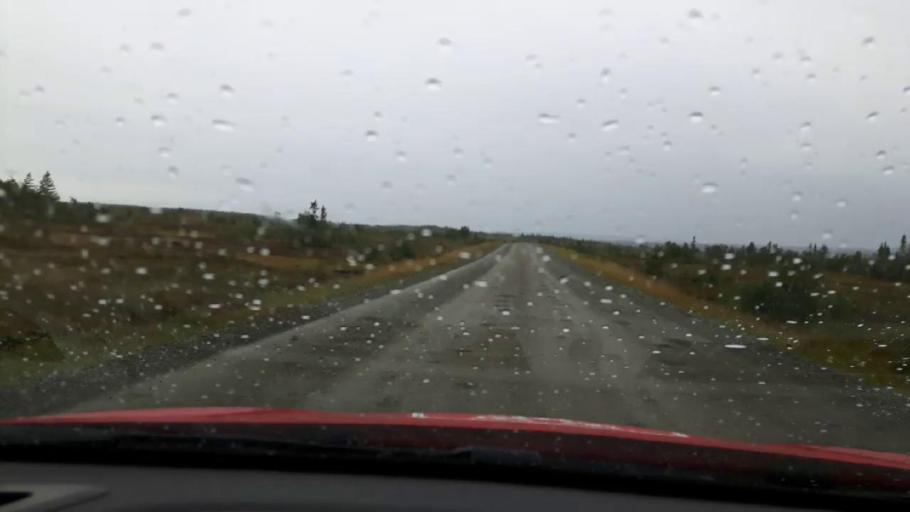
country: NO
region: Nord-Trondelag
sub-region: Meraker
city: Meraker
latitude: 63.6041
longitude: 12.2769
